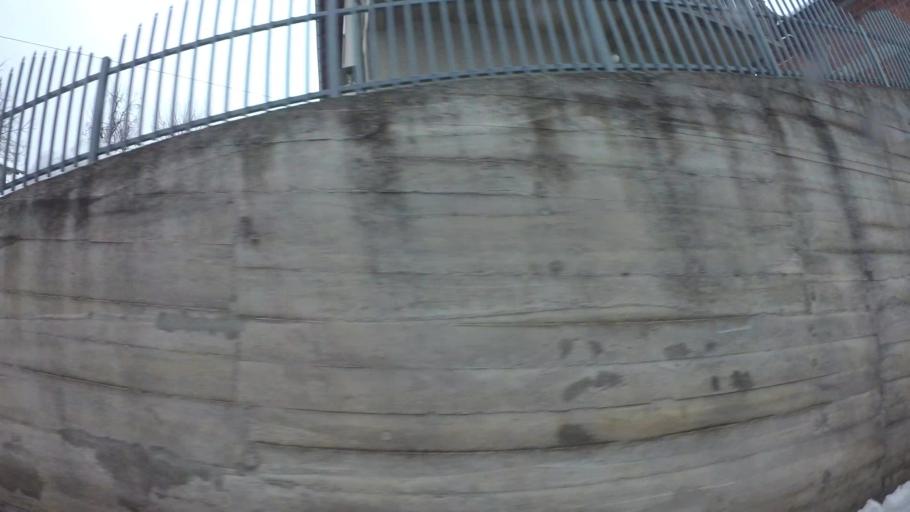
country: BA
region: Federation of Bosnia and Herzegovina
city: Hadzici
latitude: 43.8443
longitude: 18.2600
